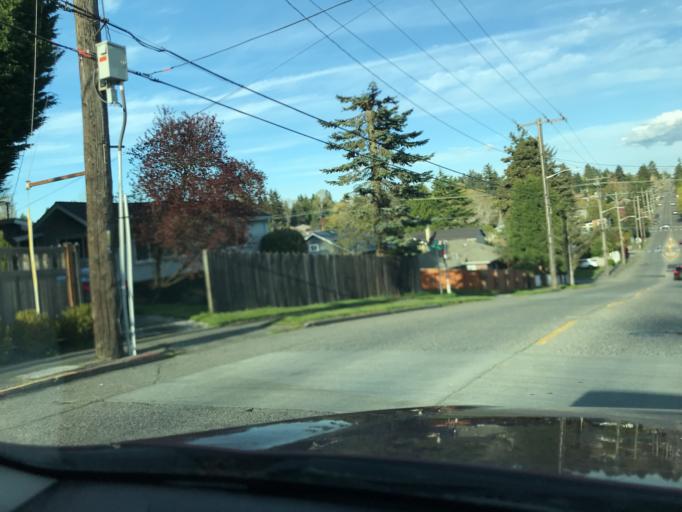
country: US
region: Washington
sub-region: King County
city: Inglewood-Finn Hill
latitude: 47.6754
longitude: -122.2886
